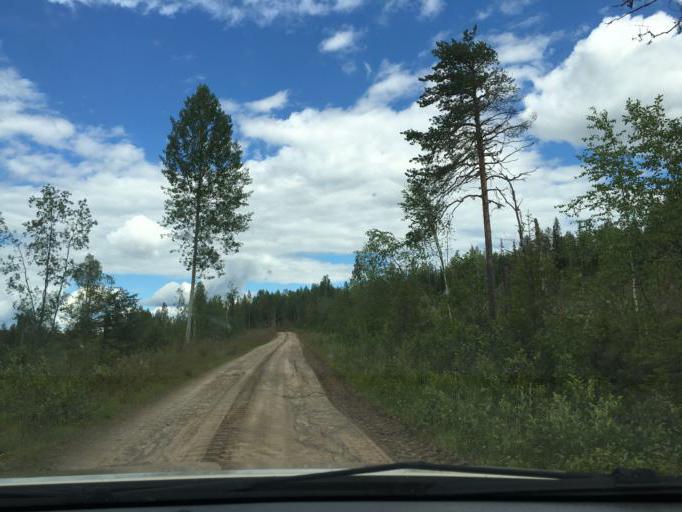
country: SE
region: Norrbotten
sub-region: Overkalix Kommun
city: OEverkalix
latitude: 66.1391
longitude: 22.7838
